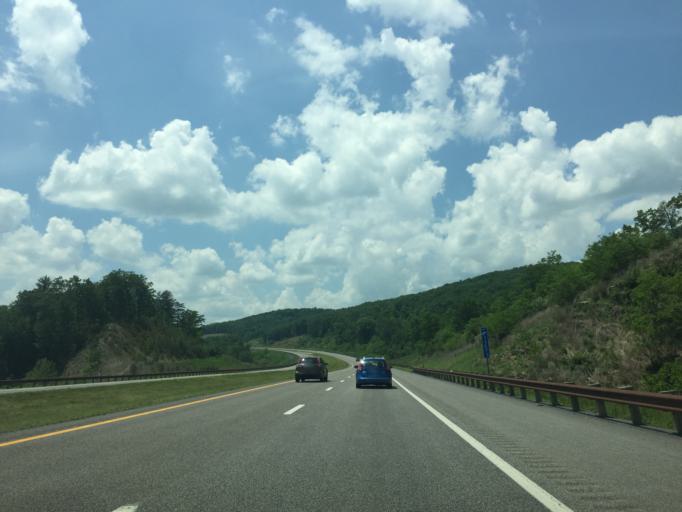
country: US
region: Virginia
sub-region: Shenandoah County
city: Woodstock
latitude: 39.0659
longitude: -78.6664
